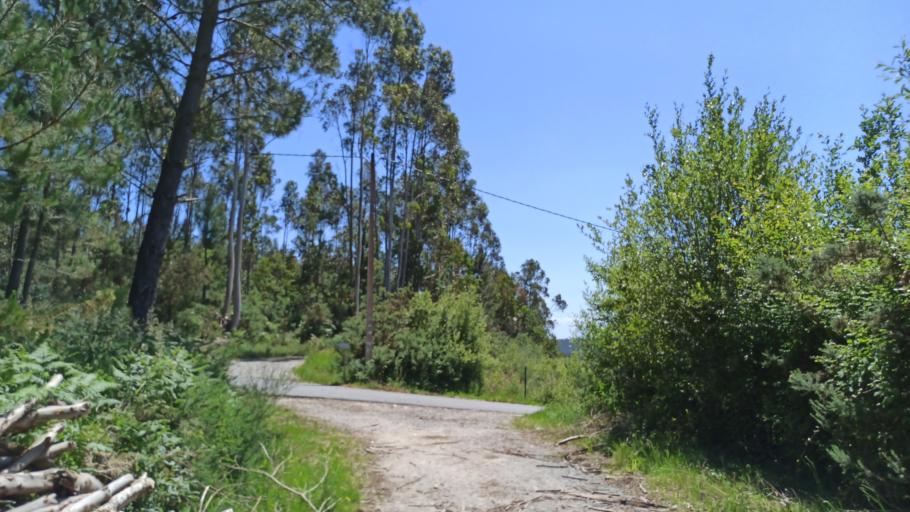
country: ES
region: Galicia
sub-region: Provincia da Coruna
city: Negreira
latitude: 42.9138
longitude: -8.7236
